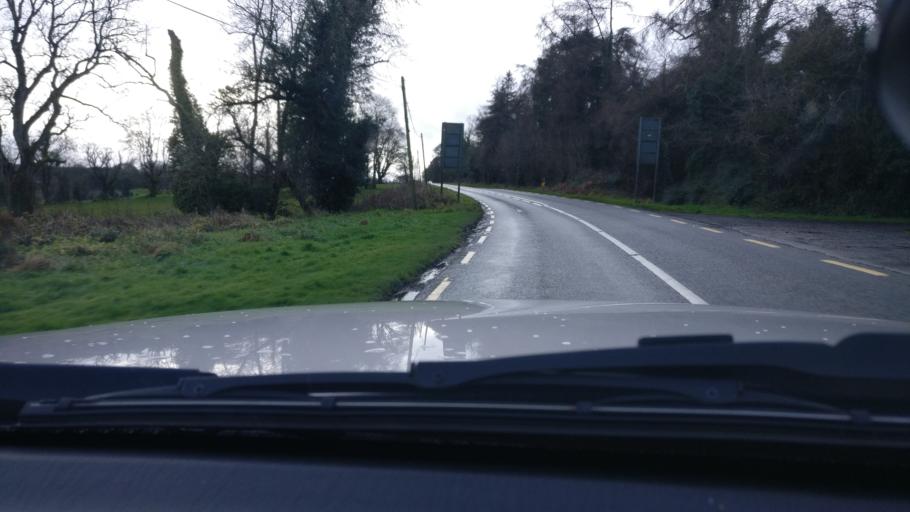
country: IE
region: Leinster
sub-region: An Iarmhi
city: Moate
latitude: 53.6299
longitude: -7.6924
